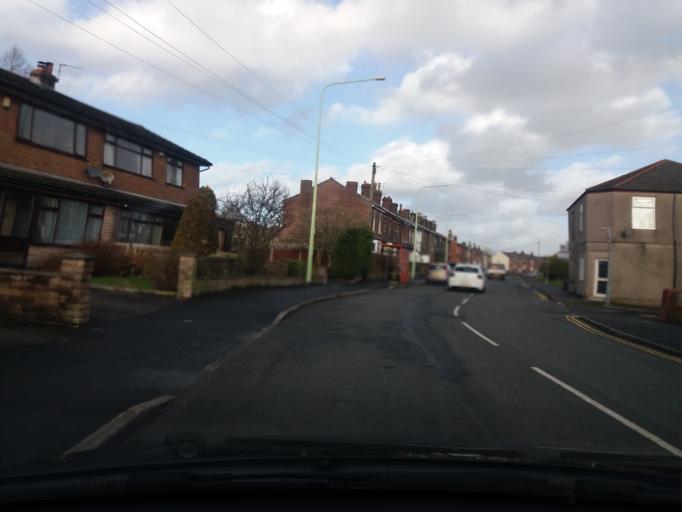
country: GB
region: England
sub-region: Lancashire
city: Adlington
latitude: 53.6102
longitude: -2.6143
